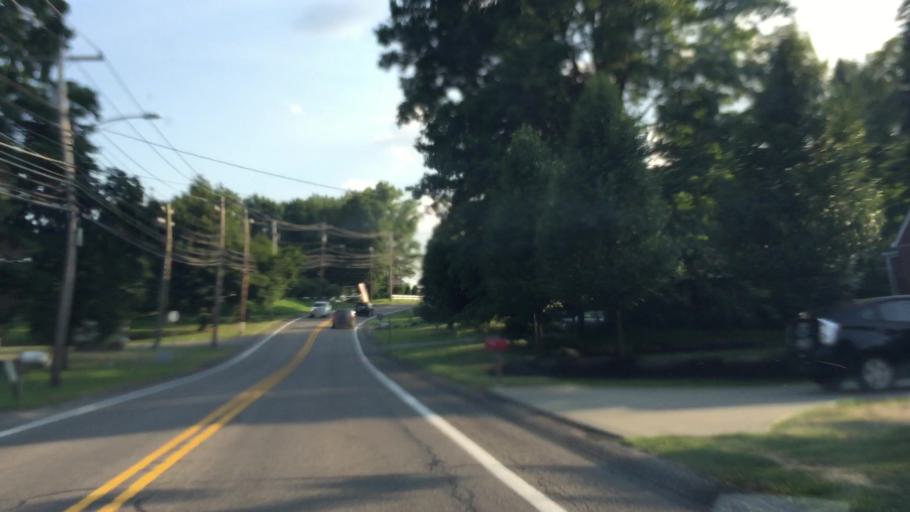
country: US
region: Pennsylvania
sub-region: Allegheny County
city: Bridgeville
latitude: 40.3453
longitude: -80.1146
